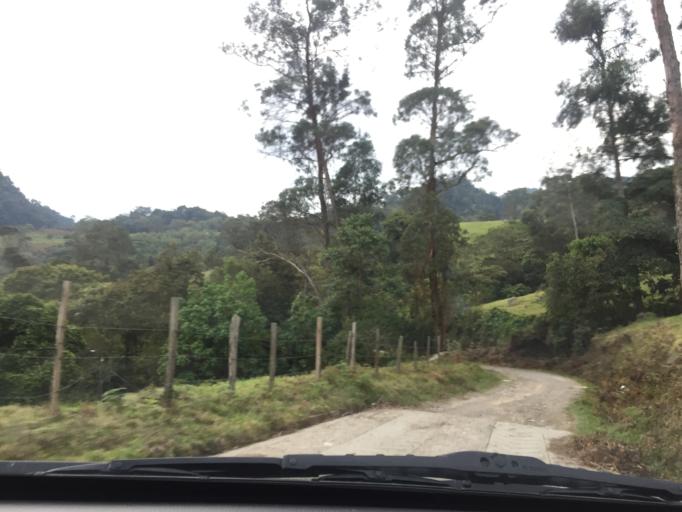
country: CO
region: Cundinamarca
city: Bojaca
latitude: 4.6818
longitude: -74.3749
